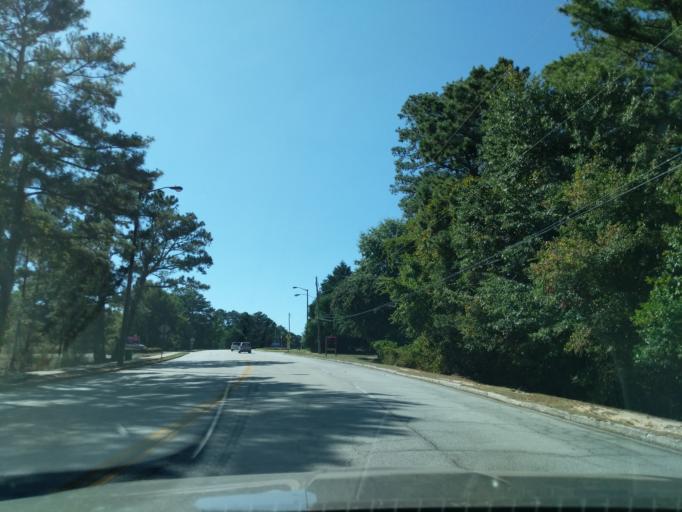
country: US
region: Georgia
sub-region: DeKalb County
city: Stone Mountain
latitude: 33.8136
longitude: -84.1407
